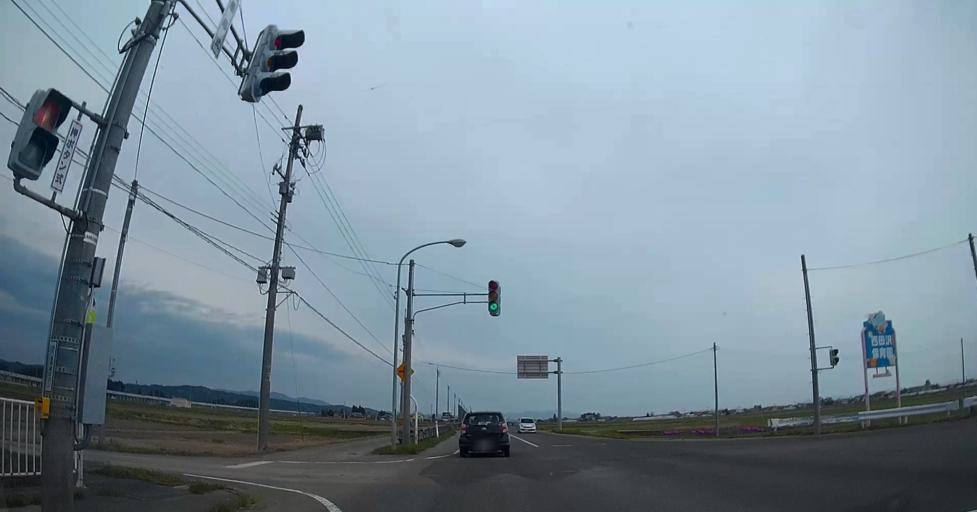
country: JP
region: Aomori
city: Aomori Shi
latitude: 40.8625
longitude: 140.6810
